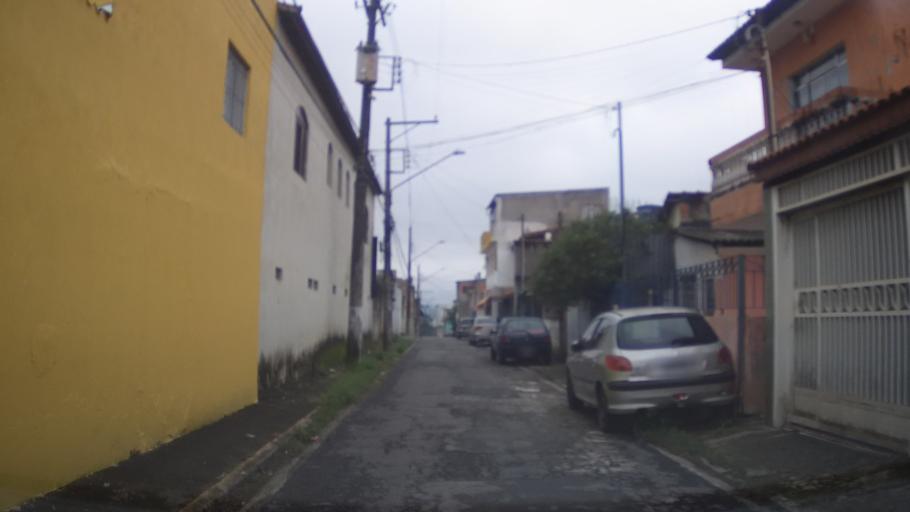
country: BR
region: Sao Paulo
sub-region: Guarulhos
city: Guarulhos
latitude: -23.5035
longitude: -46.5554
